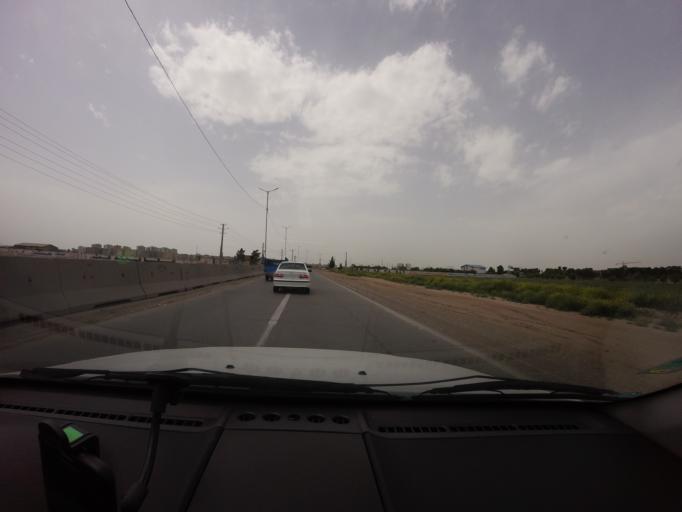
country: IR
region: Tehran
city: Eslamshahr
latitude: 35.5127
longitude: 51.2413
